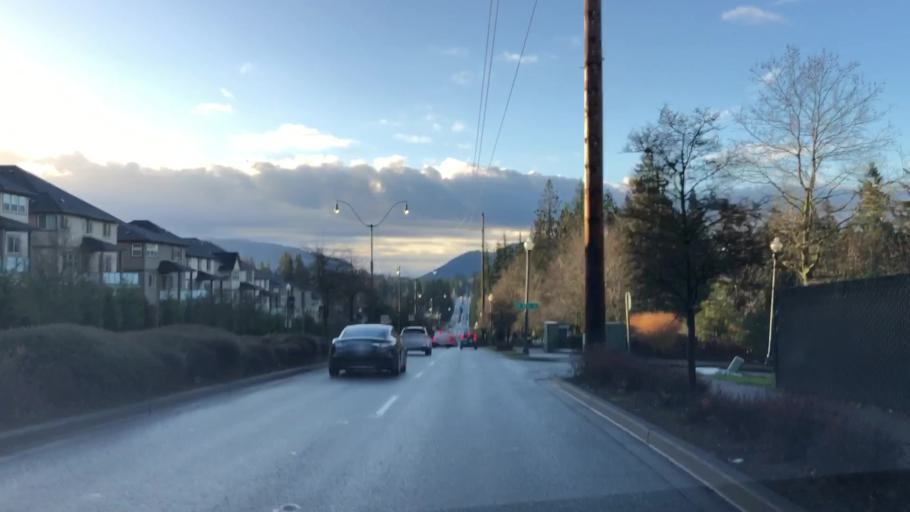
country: US
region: Washington
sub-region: King County
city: City of Sammamish
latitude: 47.5949
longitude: -122.0356
